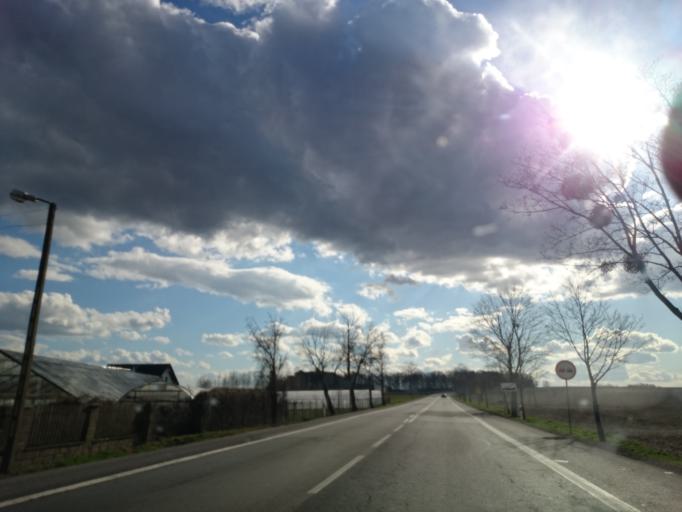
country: PL
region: Opole Voivodeship
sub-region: Powiat opolski
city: Niemodlin
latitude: 50.6371
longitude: 17.6035
